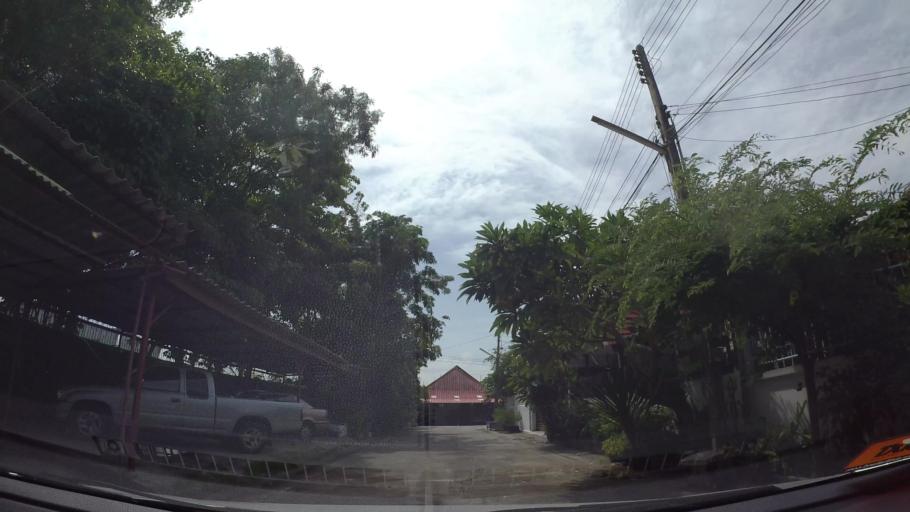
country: TH
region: Chon Buri
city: Chon Buri
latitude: 13.3265
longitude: 100.9498
